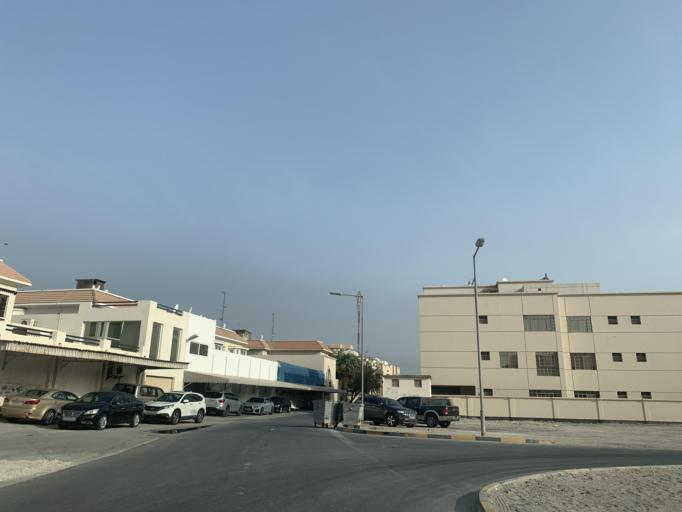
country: BH
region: Northern
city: Madinat `Isa
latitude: 26.1933
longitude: 50.5646
